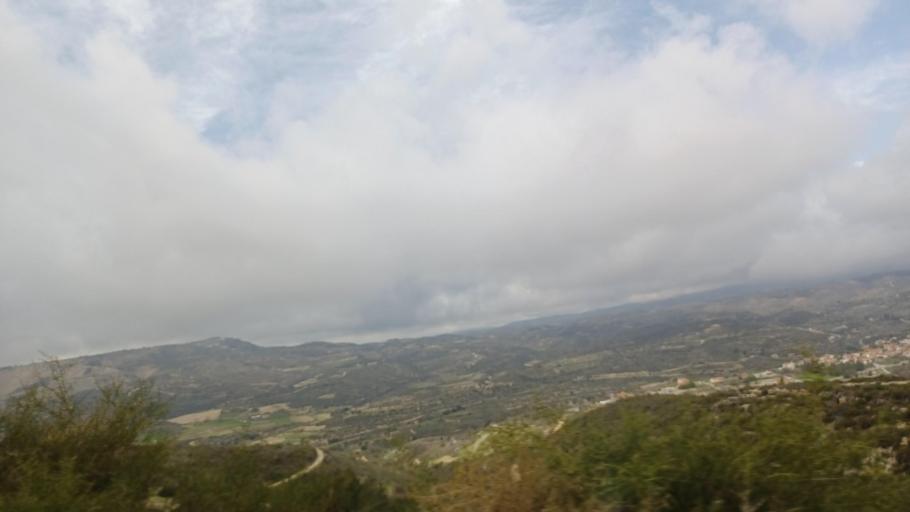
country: CY
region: Limassol
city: Pachna
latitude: 34.7685
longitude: 32.8304
